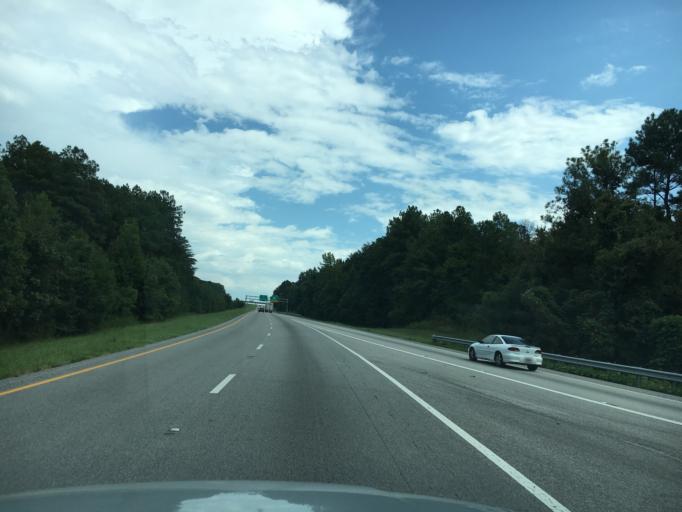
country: US
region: South Carolina
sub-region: Laurens County
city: Clinton
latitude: 34.5117
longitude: -81.8687
